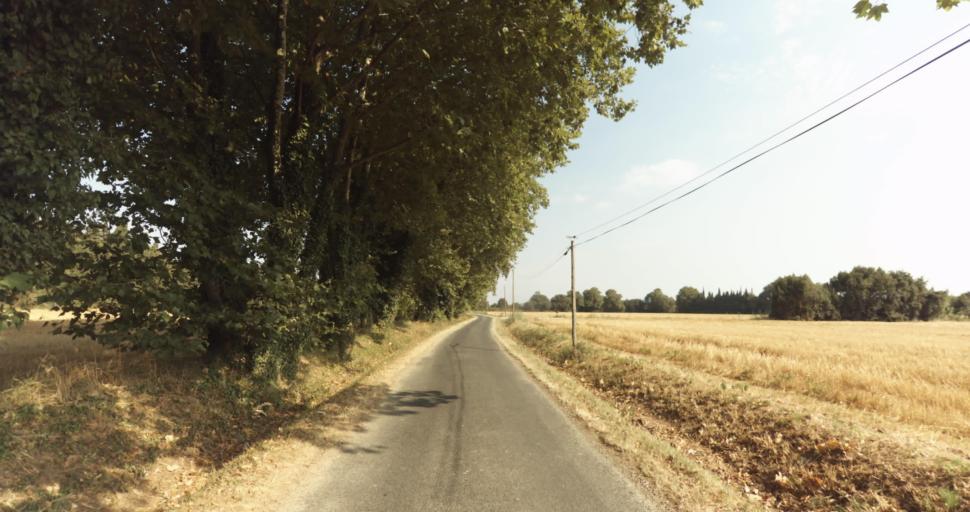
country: FR
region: Languedoc-Roussillon
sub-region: Departement des Pyrenees-Orientales
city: Latour-Bas-Elne
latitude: 42.6073
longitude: 3.0217
